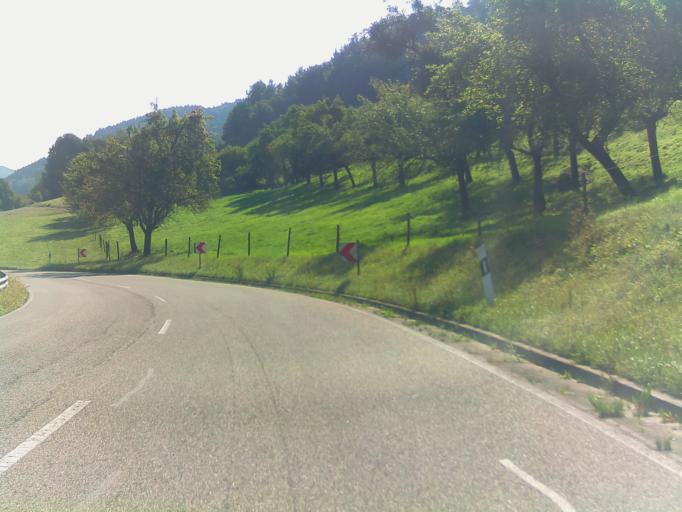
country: DE
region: Baden-Wuerttemberg
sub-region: Karlsruhe Region
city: Heddesbach
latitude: 49.4753
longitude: 8.8333
